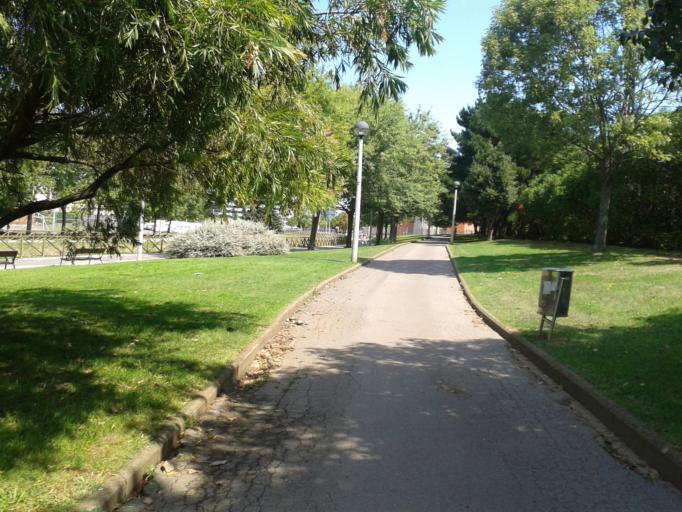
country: ES
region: Asturias
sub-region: Province of Asturias
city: Natahoyo
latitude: 43.5365
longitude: -5.6791
